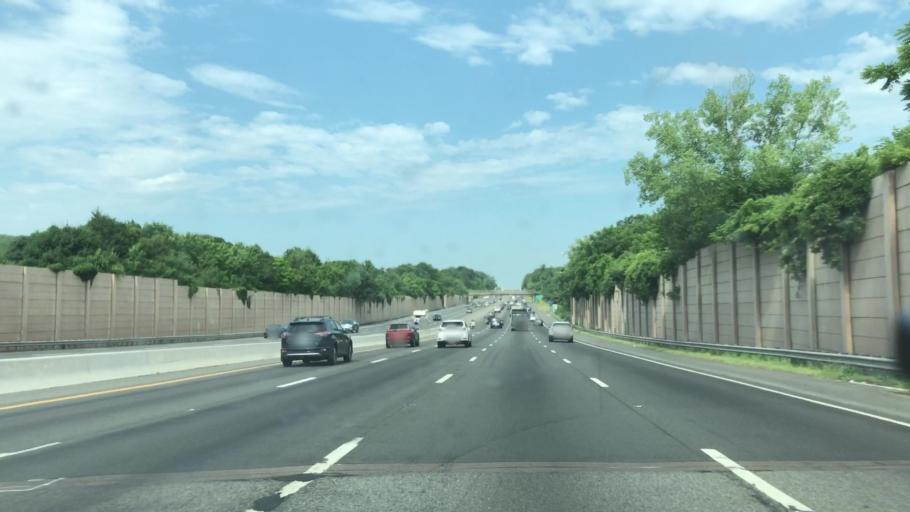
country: US
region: New Jersey
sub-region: Morris County
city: Rockaway
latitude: 40.9113
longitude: -74.5199
